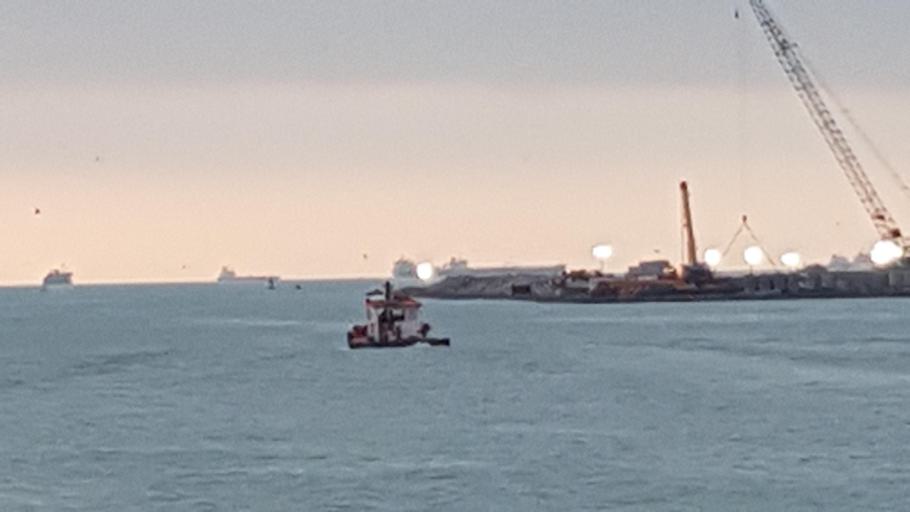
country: PE
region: Callao
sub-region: Callao
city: Callao
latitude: -12.0589
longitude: -77.1494
